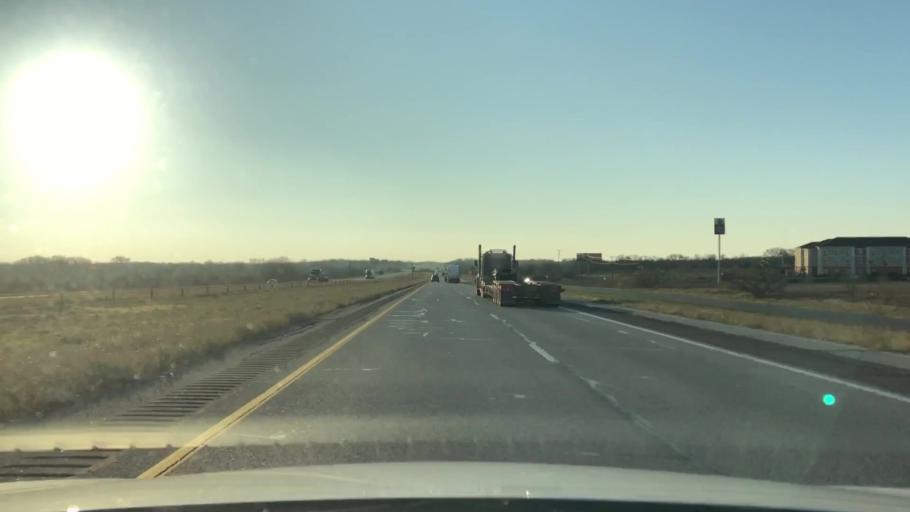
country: US
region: Texas
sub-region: Caldwell County
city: Luling
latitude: 29.6524
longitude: -97.5937
